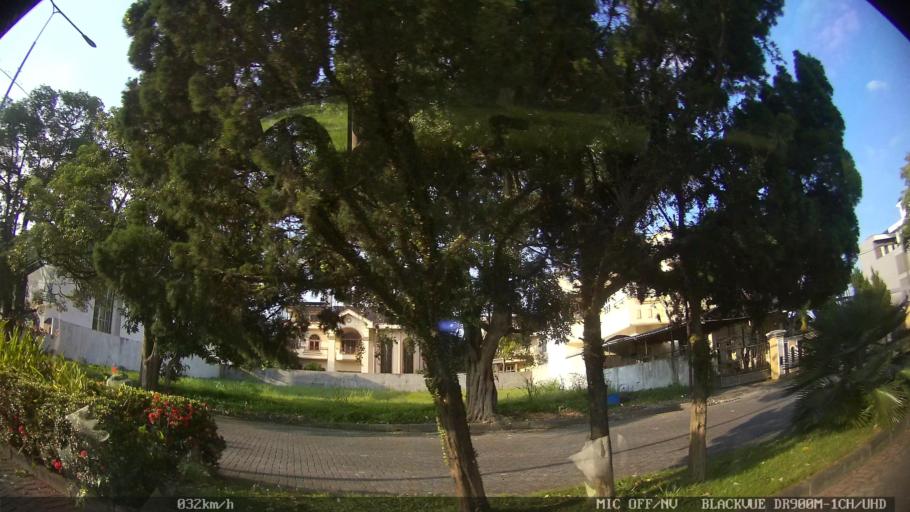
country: ID
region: North Sumatra
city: Medan
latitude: 3.6241
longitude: 98.6573
